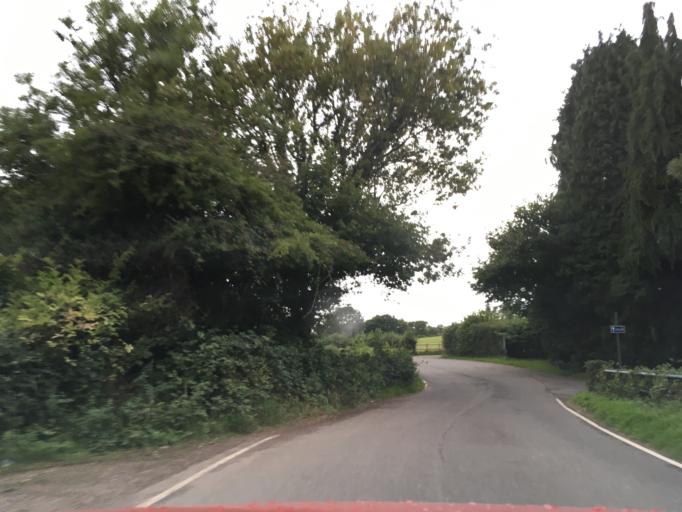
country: GB
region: Wales
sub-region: Monmouthshire
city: Llangybi
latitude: 51.6683
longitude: -2.8695
